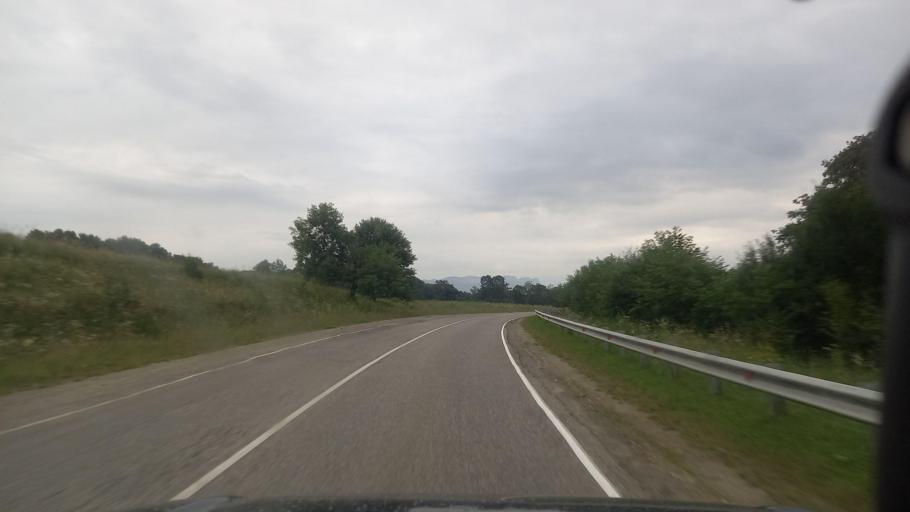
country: RU
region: Karachayevo-Cherkesiya
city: Mednogorskiy
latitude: 43.9434
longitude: 41.1286
